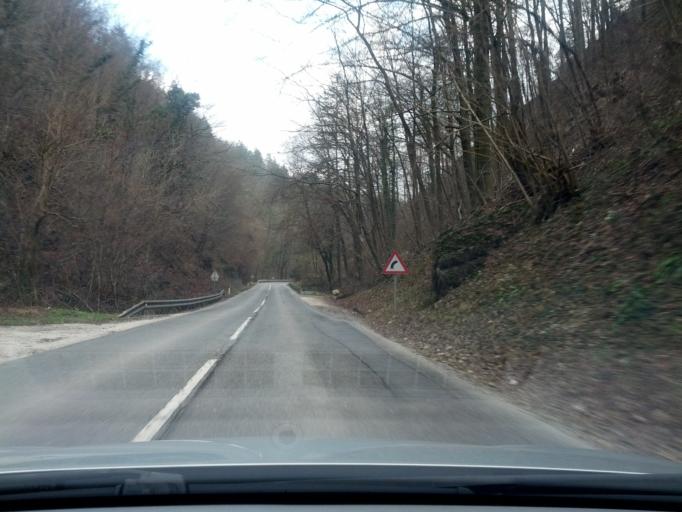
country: SI
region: Lasko
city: Lasko
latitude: 46.1329
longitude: 15.1845
